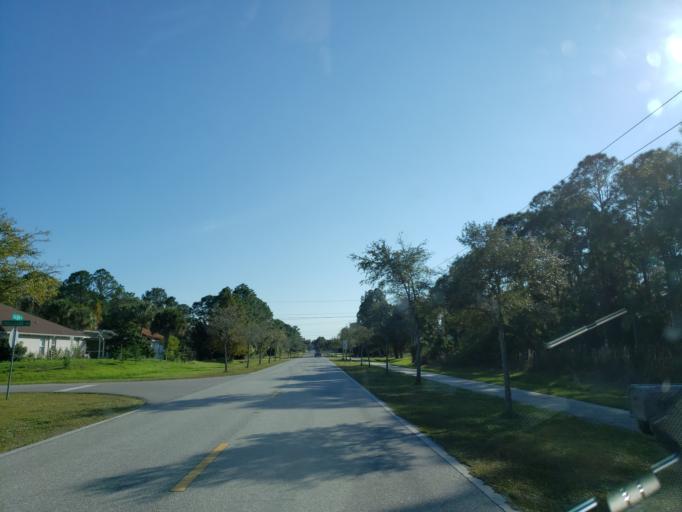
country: US
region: Florida
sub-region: Sarasota County
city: North Port
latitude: 27.0800
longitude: -82.1952
